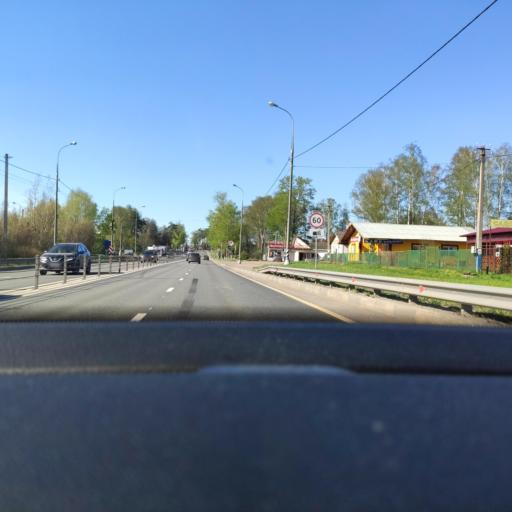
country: RU
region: Moskovskaya
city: Dedenevo
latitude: 56.2298
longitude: 37.5273
